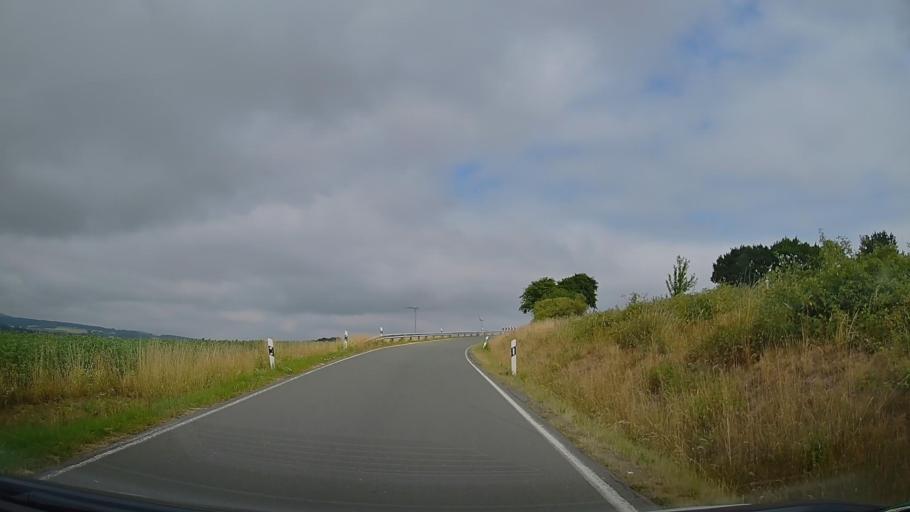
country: DE
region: North Rhine-Westphalia
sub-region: Regierungsbezirk Detmold
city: Barntrup
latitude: 52.0718
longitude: 9.1332
